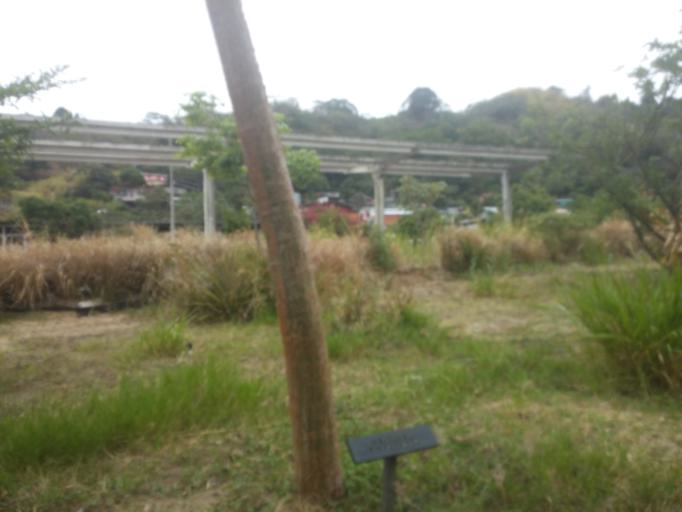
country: CR
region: San Jose
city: Patarra
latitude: 9.8878
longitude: -84.0323
